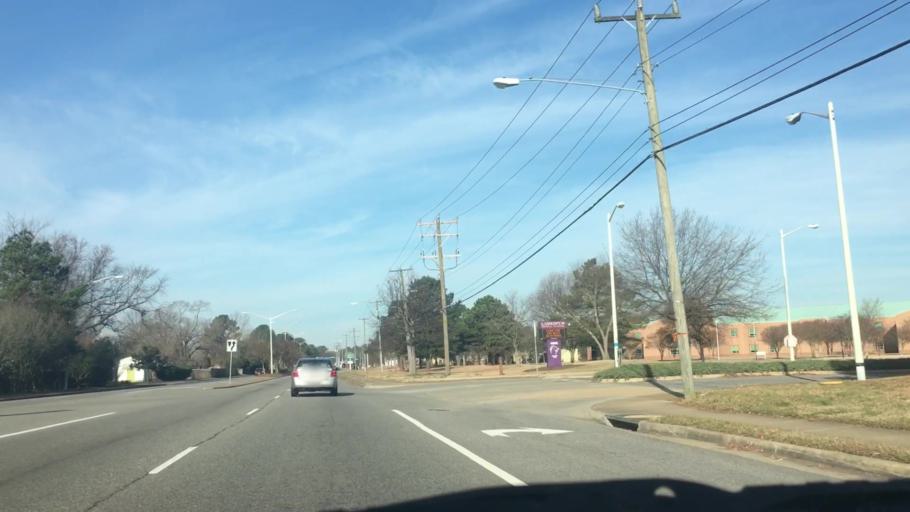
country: US
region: Virginia
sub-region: City of Chesapeake
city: Chesapeake
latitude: 36.8131
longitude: -76.1416
